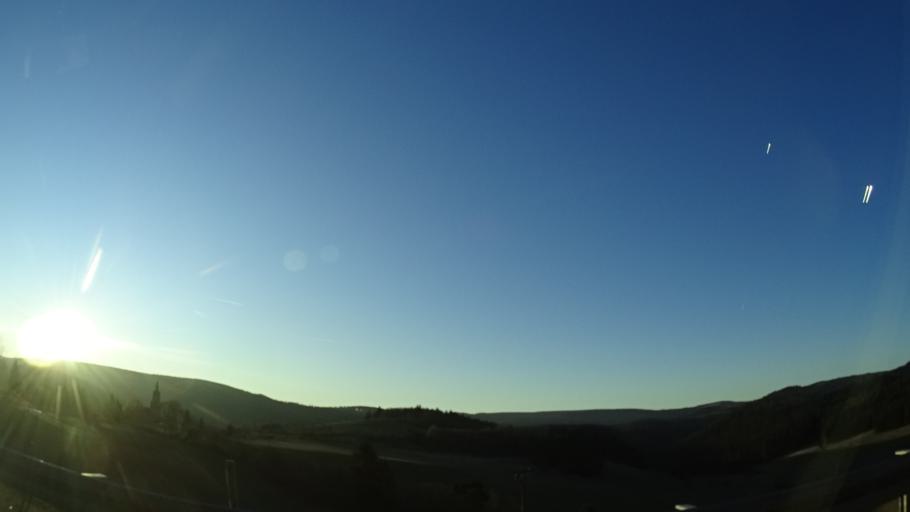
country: DE
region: Thuringia
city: Grafenthal
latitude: 50.5377
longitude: 11.2964
